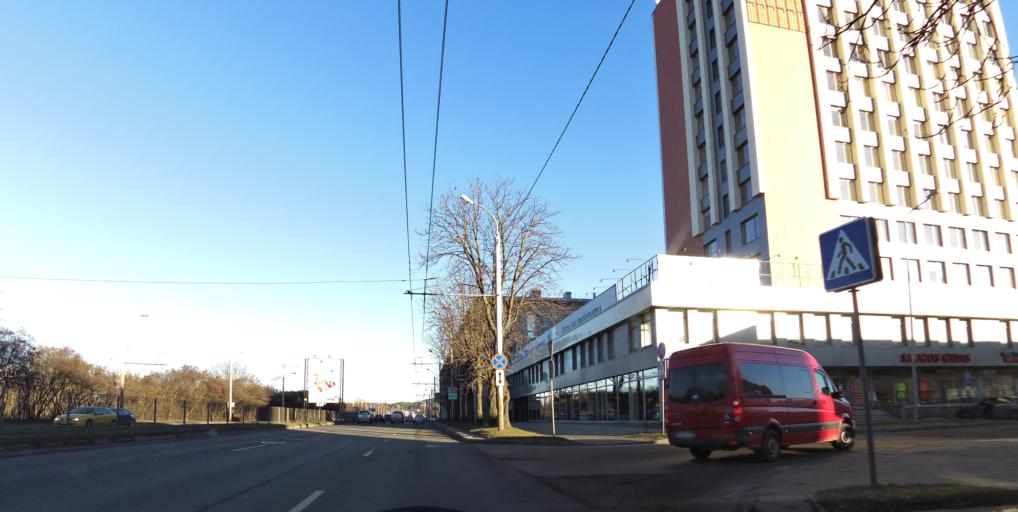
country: LT
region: Vilnius County
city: Lazdynai
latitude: 54.6525
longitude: 25.2213
